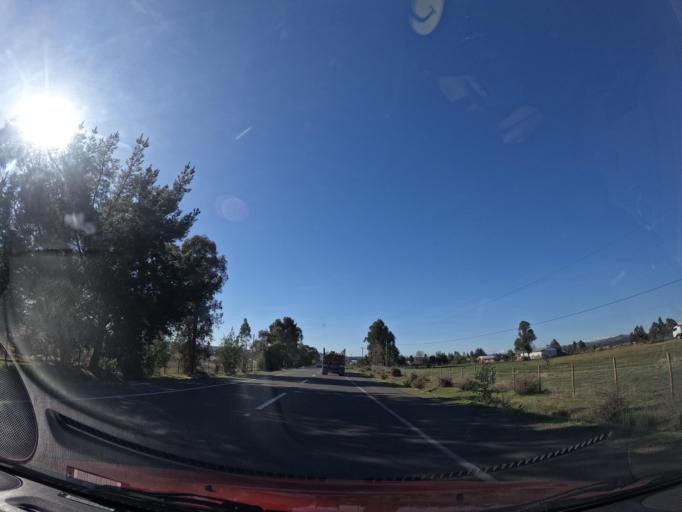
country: CL
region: Maule
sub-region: Provincia de Cauquenes
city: Cauquenes
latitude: -35.9609
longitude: -72.2185
